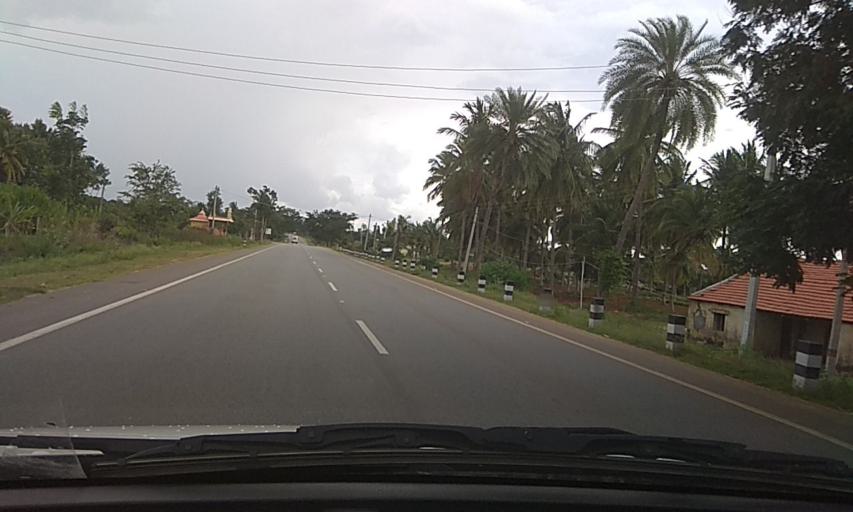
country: IN
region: Karnataka
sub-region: Tumkur
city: Kunigal
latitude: 12.8855
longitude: 77.0442
